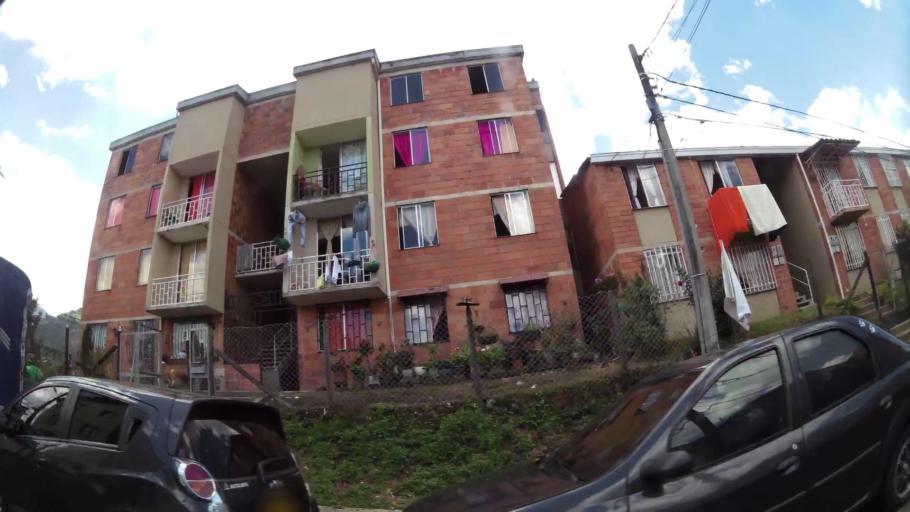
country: CO
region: Antioquia
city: La Estrella
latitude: 6.1535
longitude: -75.6396
